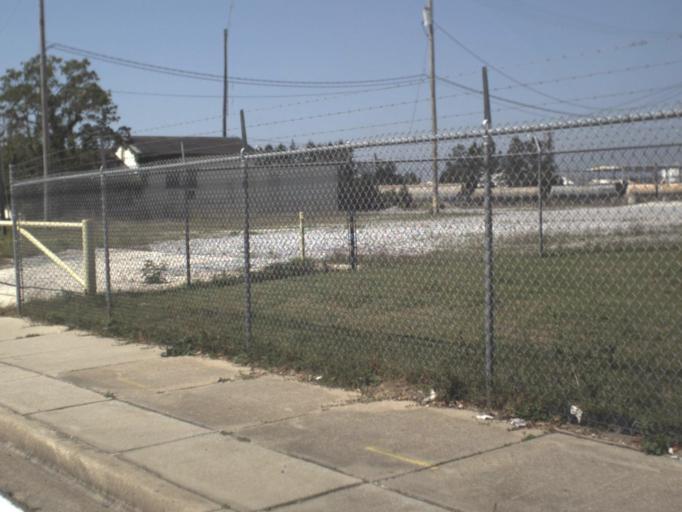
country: US
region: Florida
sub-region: Escambia County
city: Pensacola
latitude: 30.4098
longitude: -87.2419
